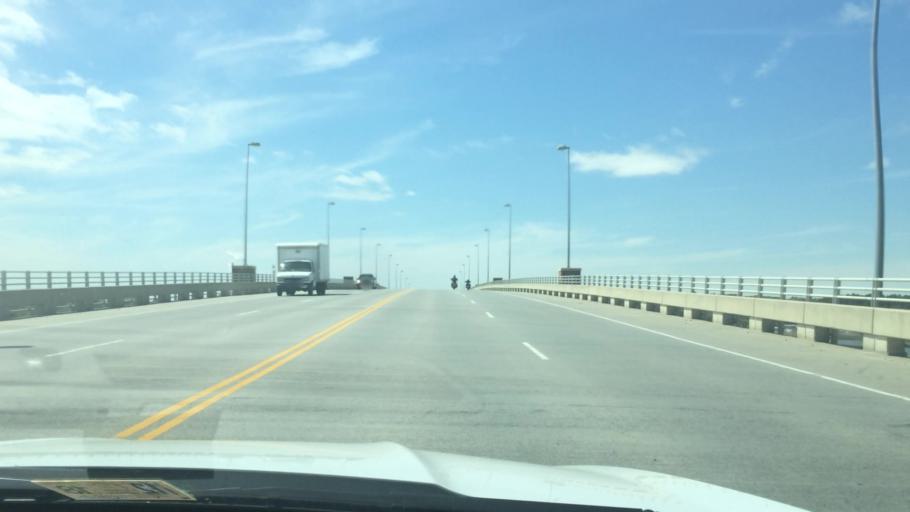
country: US
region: Virginia
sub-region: King William County
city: West Point
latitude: 37.5367
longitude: -76.7865
